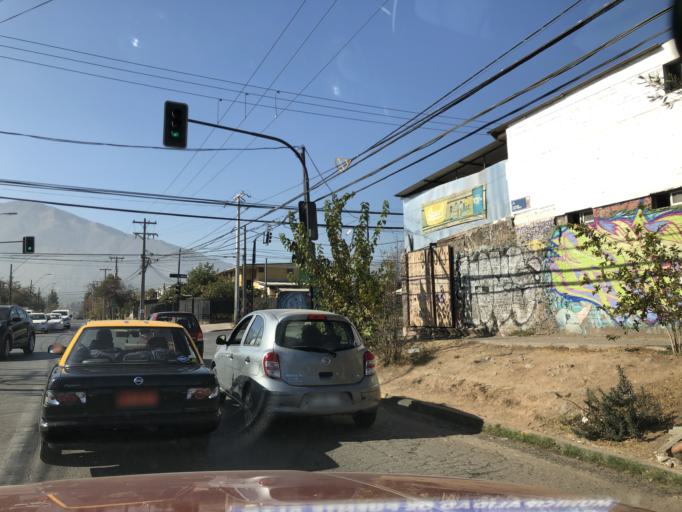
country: CL
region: Santiago Metropolitan
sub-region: Provincia de Cordillera
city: Puente Alto
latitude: -33.5676
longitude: -70.5674
